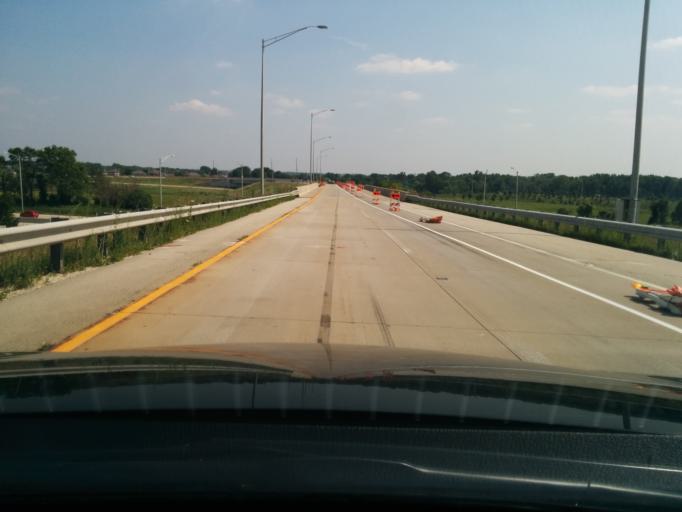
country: US
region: Illinois
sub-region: Will County
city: New Lenox
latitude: 41.5391
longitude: -87.9627
